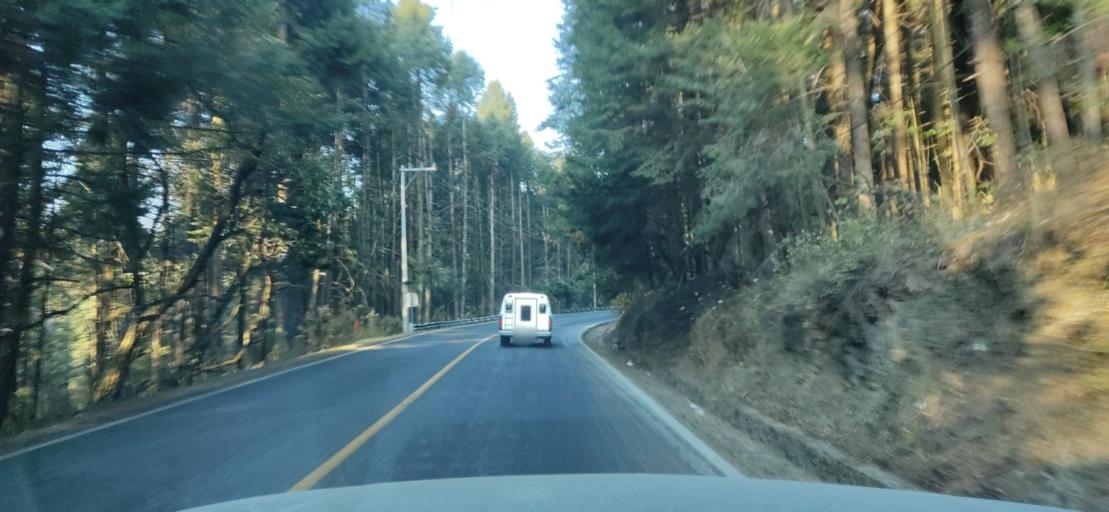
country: MX
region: Mexico
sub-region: Ocoyoacac
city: San Jeronimo Acazulco
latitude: 19.2603
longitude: -99.3763
